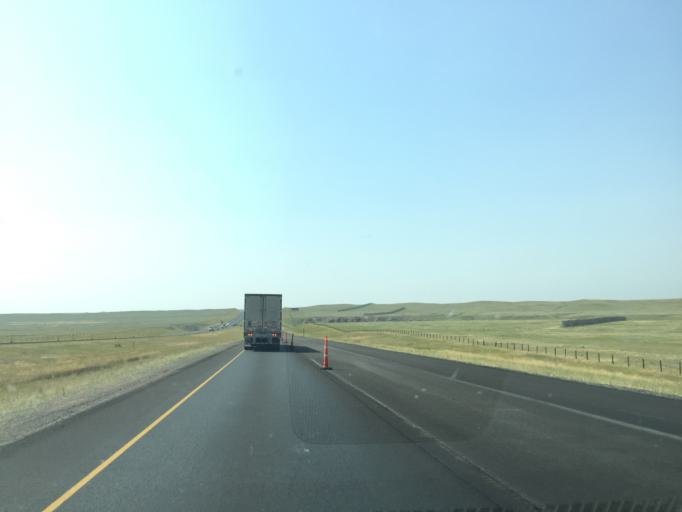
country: US
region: Wyoming
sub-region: Laramie County
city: Ranchettes
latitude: 41.3308
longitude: -104.8640
